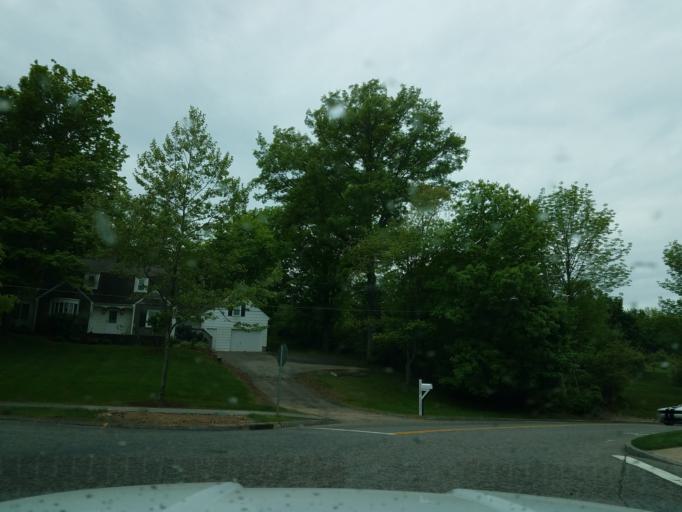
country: US
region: Connecticut
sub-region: Tolland County
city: Storrs
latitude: 41.8024
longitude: -72.2507
